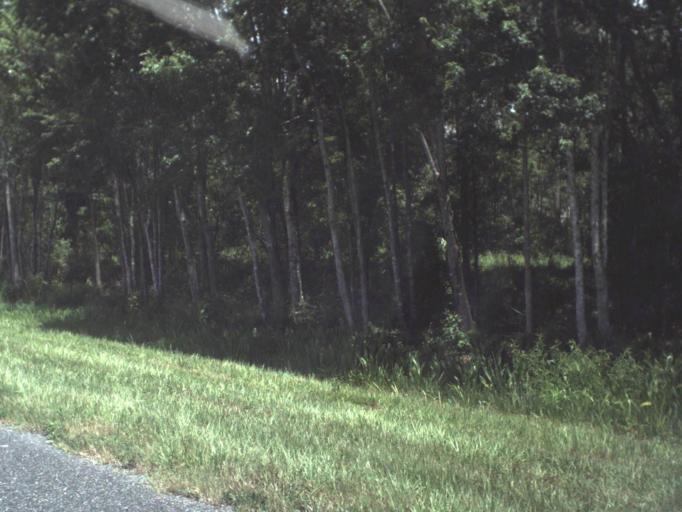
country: US
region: Florida
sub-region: Taylor County
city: Steinhatchee
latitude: 29.8234
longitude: -83.3546
